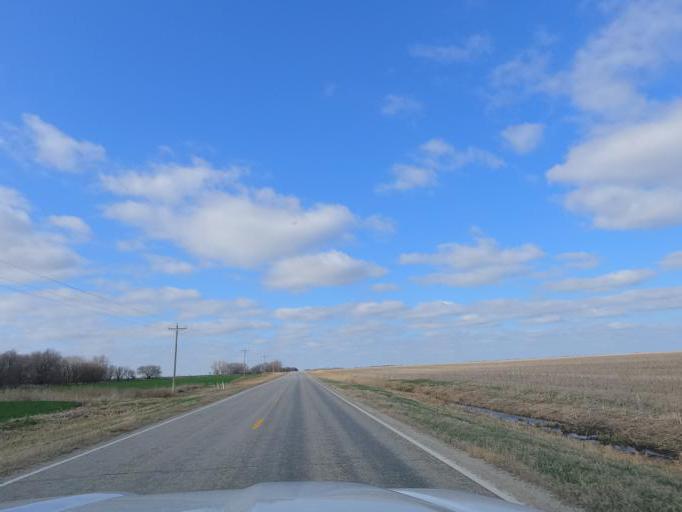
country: US
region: Kansas
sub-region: McPherson County
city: Inman
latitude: 38.1898
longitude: -97.8486
